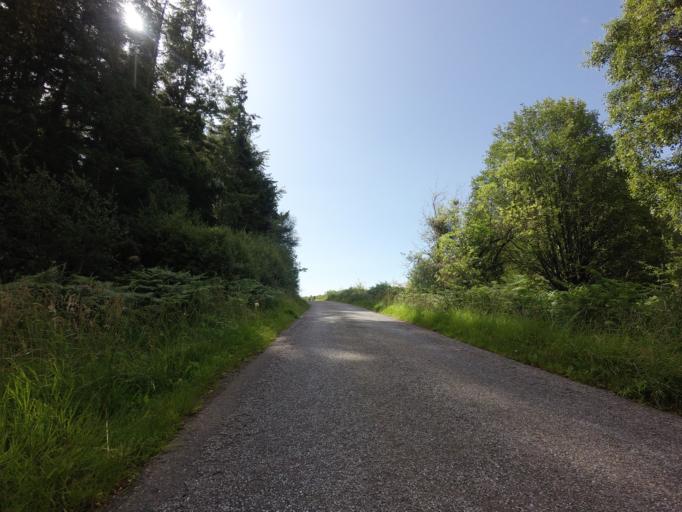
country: GB
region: Scotland
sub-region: Highland
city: Nairn
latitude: 57.5350
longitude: -3.8659
